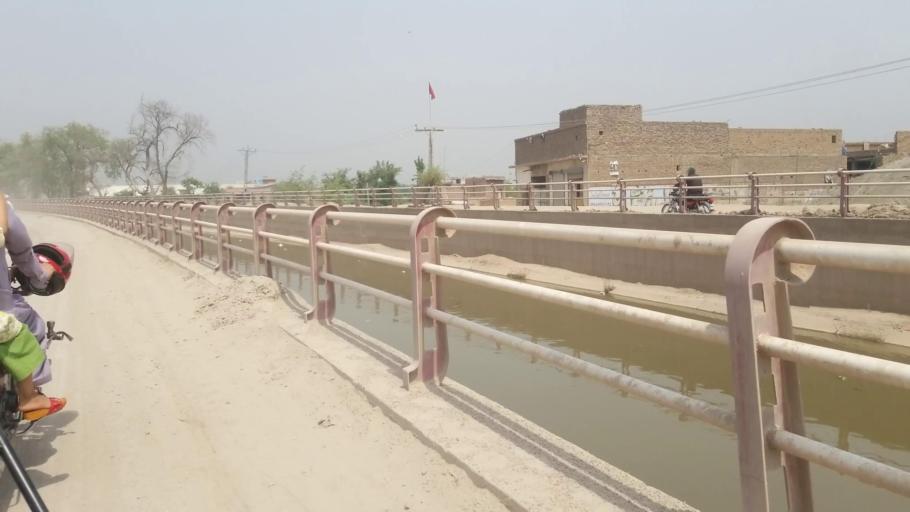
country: PK
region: Khyber Pakhtunkhwa
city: Peshawar
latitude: 33.9661
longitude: 71.5415
